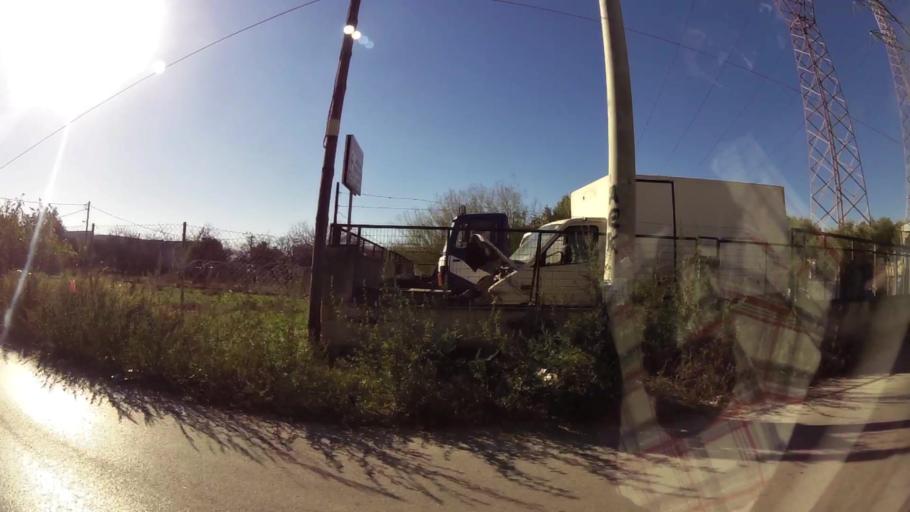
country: GR
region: Attica
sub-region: Nomarchia Anatolikis Attikis
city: Acharnes
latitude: 38.0797
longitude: 23.7508
